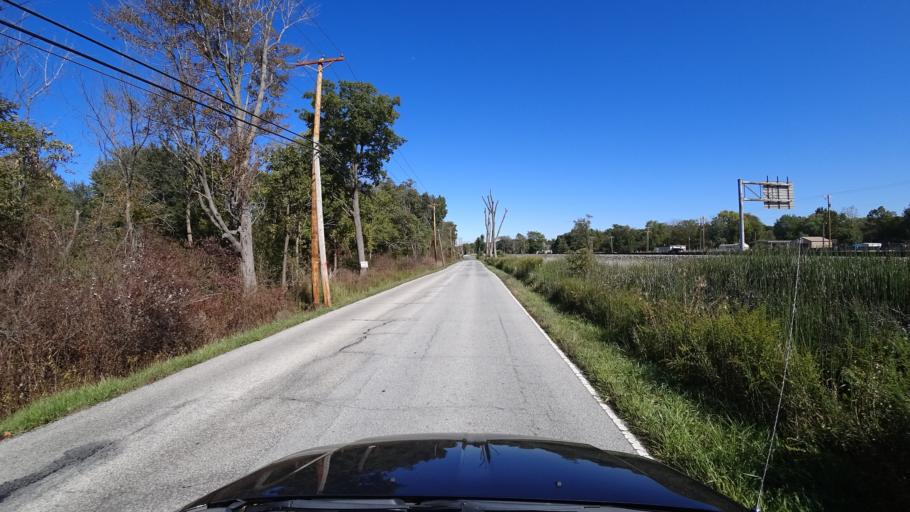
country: US
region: Indiana
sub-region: LaPorte County
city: Long Beach
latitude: 41.7494
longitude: -86.8187
